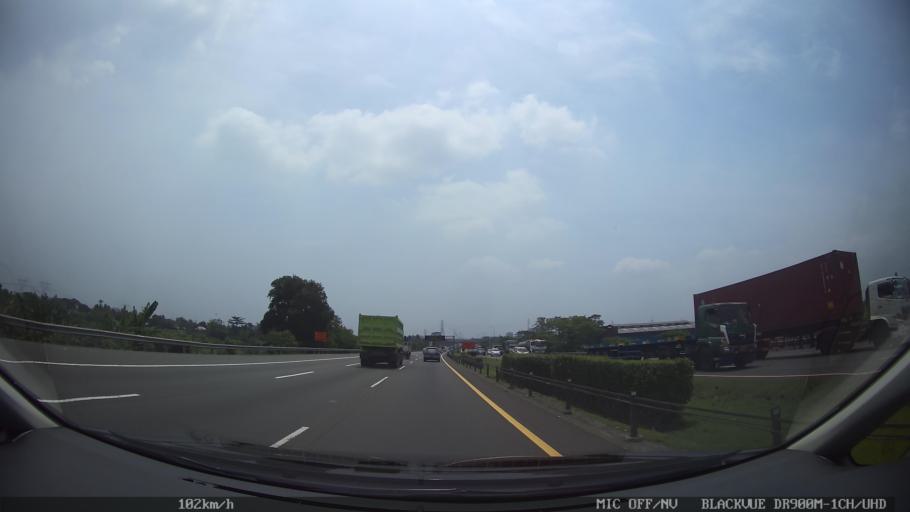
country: ID
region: West Java
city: Kresek
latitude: -6.1757
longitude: 106.3526
